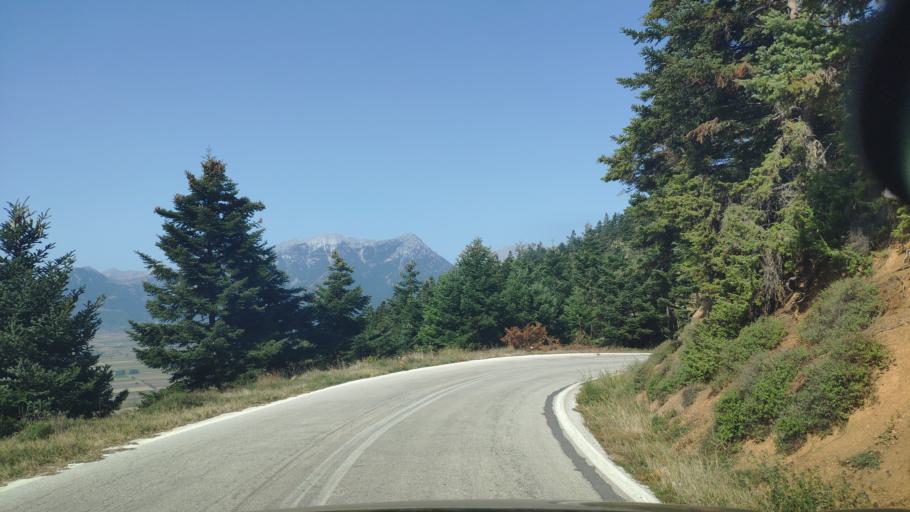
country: GR
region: West Greece
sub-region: Nomos Achaias
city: Aiyira
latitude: 37.8668
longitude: 22.3653
